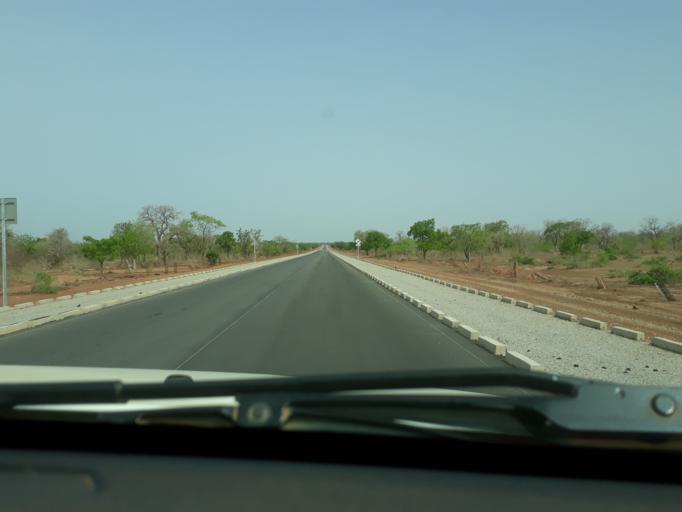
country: BF
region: Plateau-Central
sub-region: Province d'Oubritenga
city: Ziniare
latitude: 12.5501
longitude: -1.4055
